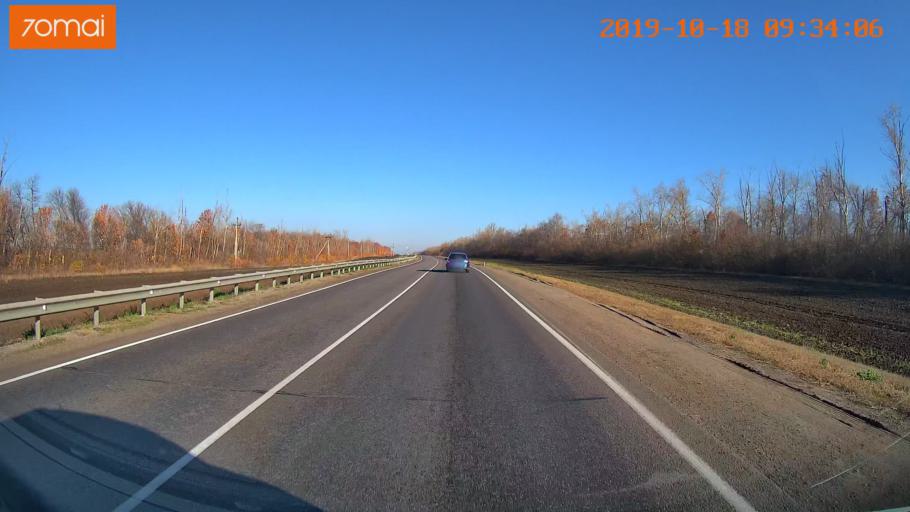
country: RU
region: Tula
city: Yefremov
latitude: 53.1753
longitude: 38.1527
